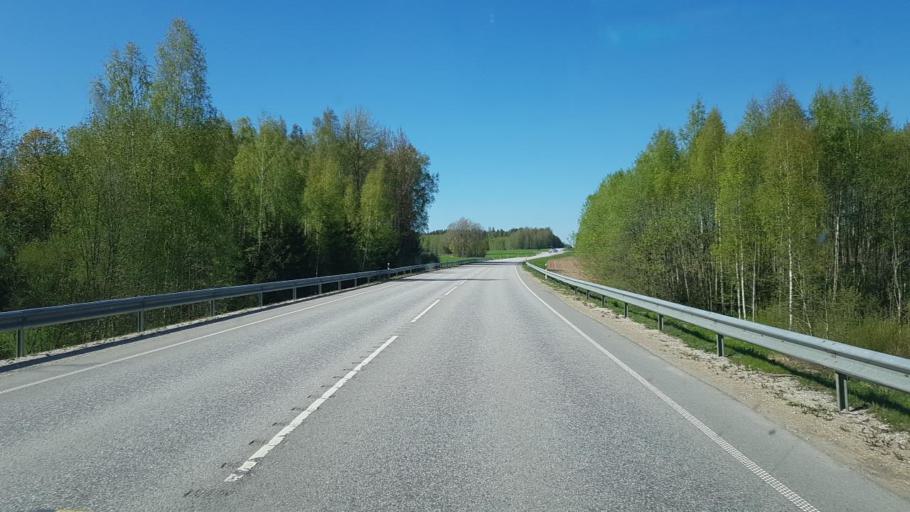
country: EE
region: Vorumaa
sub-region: Voru linn
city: Voru
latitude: 57.9275
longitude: 26.7992
